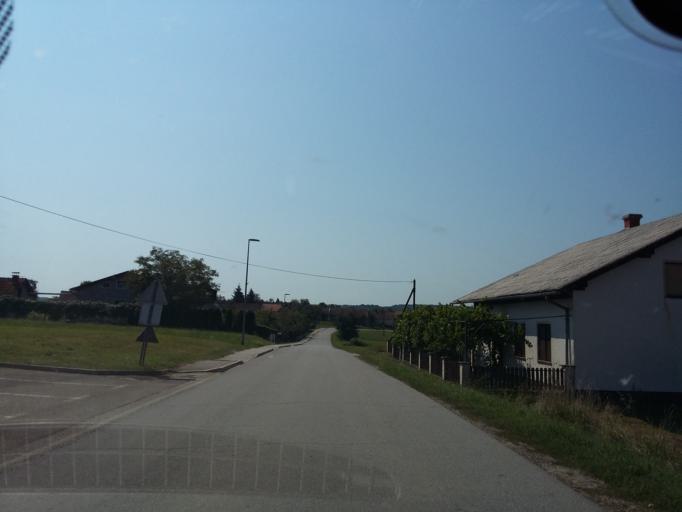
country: SI
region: Hodos-Hodos
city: Hodos
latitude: 46.8273
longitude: 16.3253
